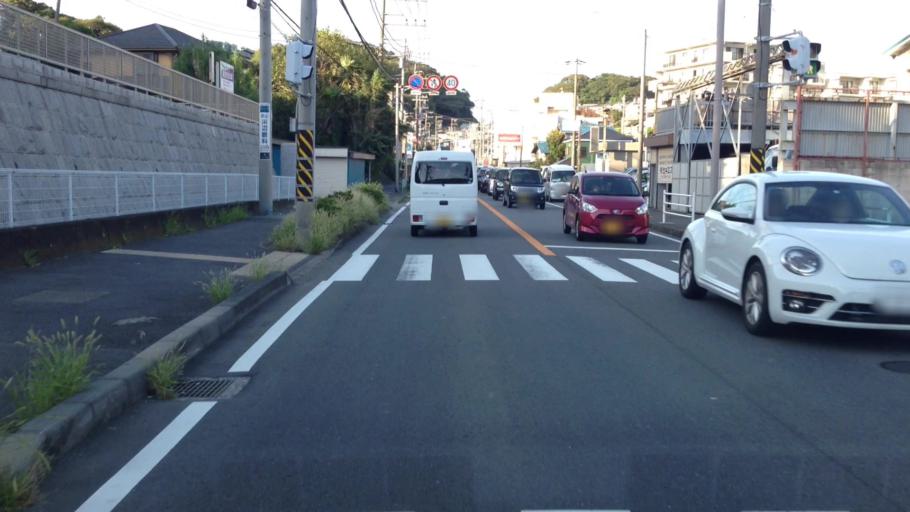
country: JP
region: Kanagawa
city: Yokosuka
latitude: 35.2278
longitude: 139.6511
